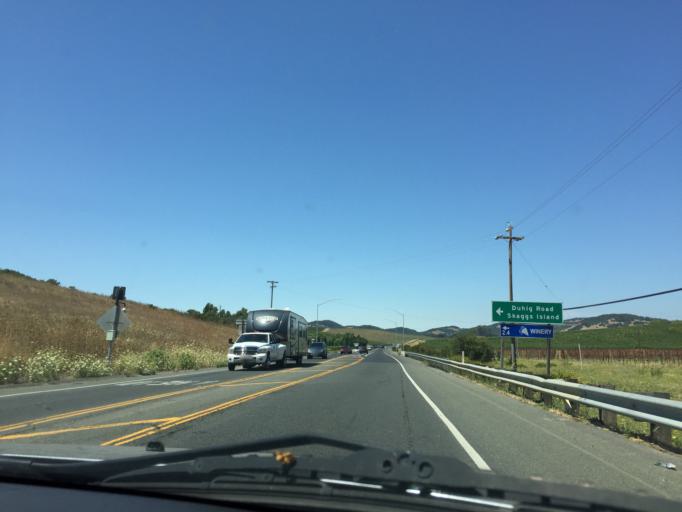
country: US
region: California
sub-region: Napa County
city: Napa
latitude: 38.2557
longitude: -122.3447
